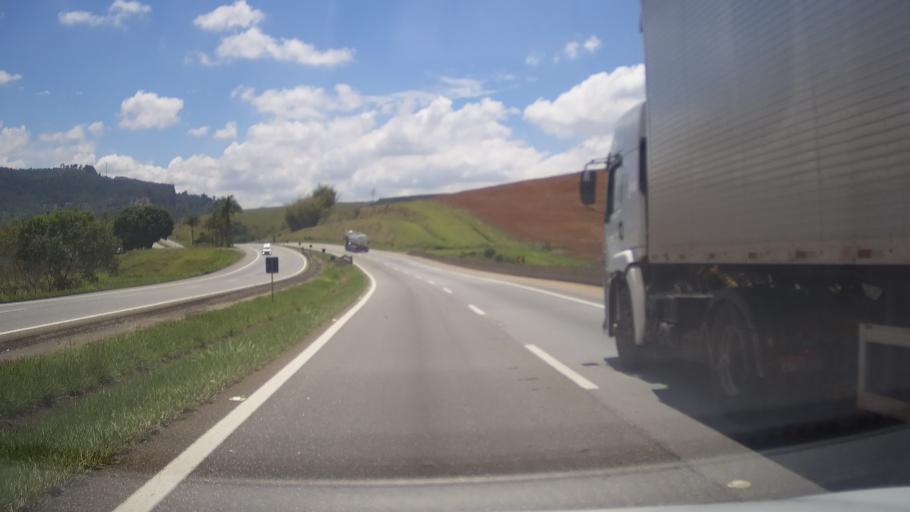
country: BR
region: Minas Gerais
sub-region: Campanha
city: Campanha
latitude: -21.8232
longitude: -45.4946
